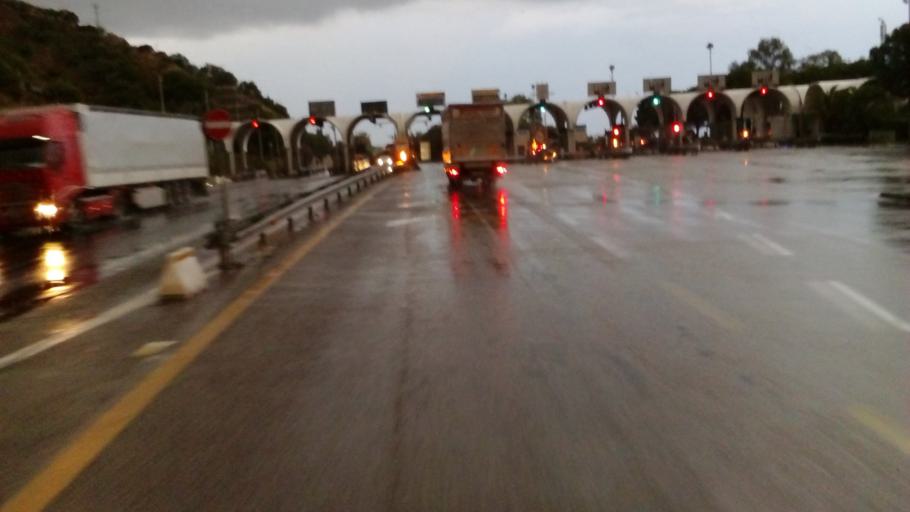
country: IT
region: Sicily
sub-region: Messina
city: Larderia
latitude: 38.1239
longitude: 15.5161
